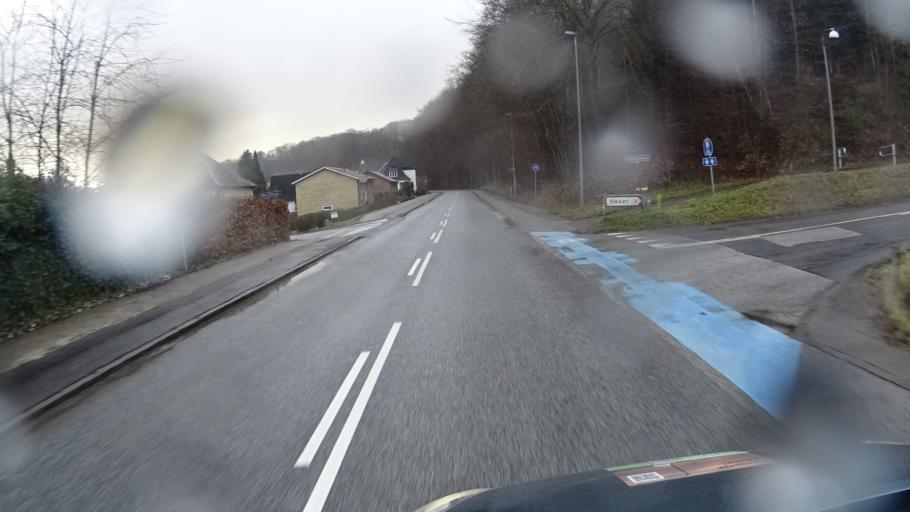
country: DK
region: South Denmark
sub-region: Vejle Kommune
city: Vejle
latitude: 55.7385
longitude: 9.5330
